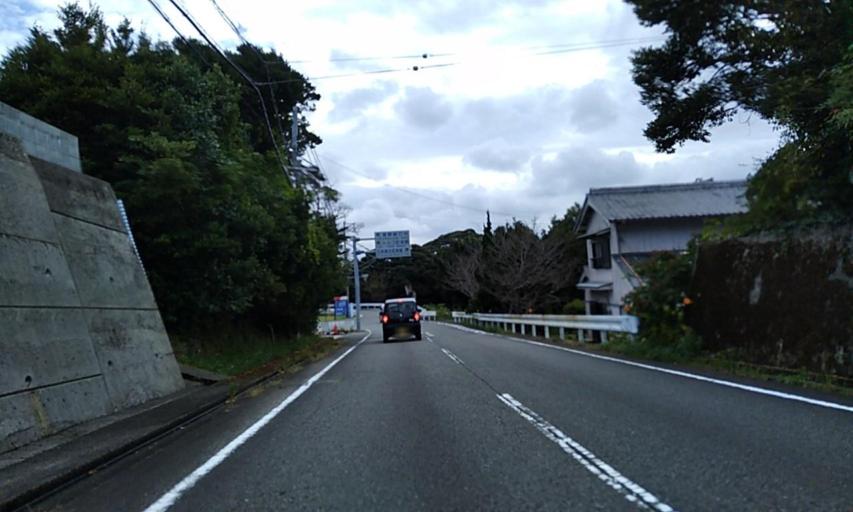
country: JP
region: Wakayama
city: Shingu
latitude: 33.4694
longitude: 135.8475
